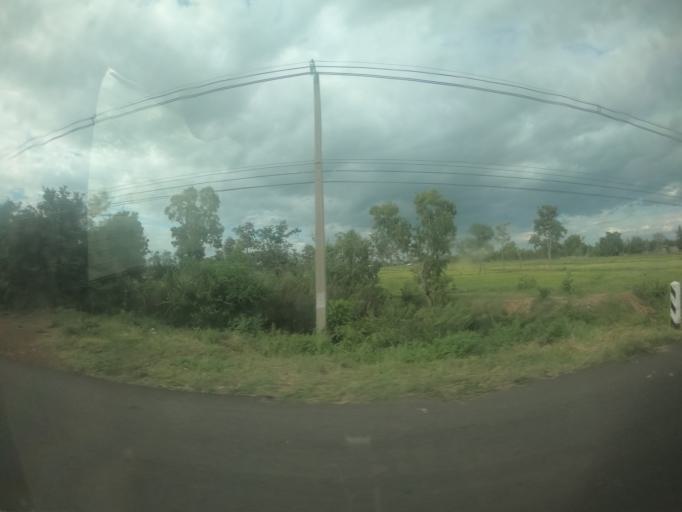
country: TH
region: Surin
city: Kap Choeng
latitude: 14.5321
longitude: 103.5295
